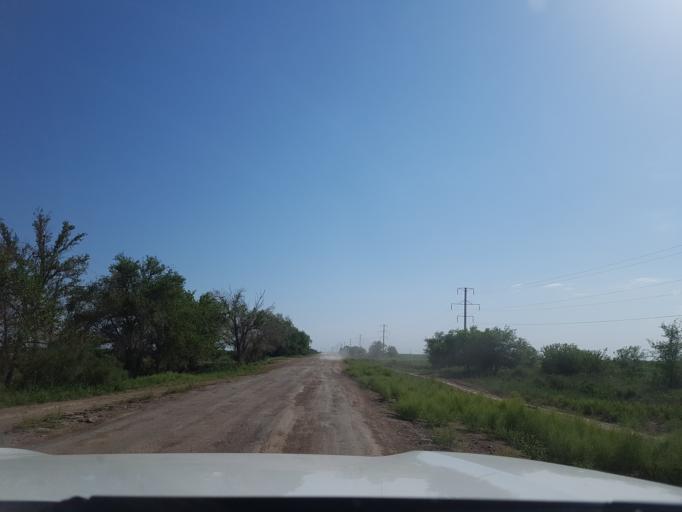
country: TM
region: Dasoguz
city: Koeneuergench
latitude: 42.1275
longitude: 58.9416
